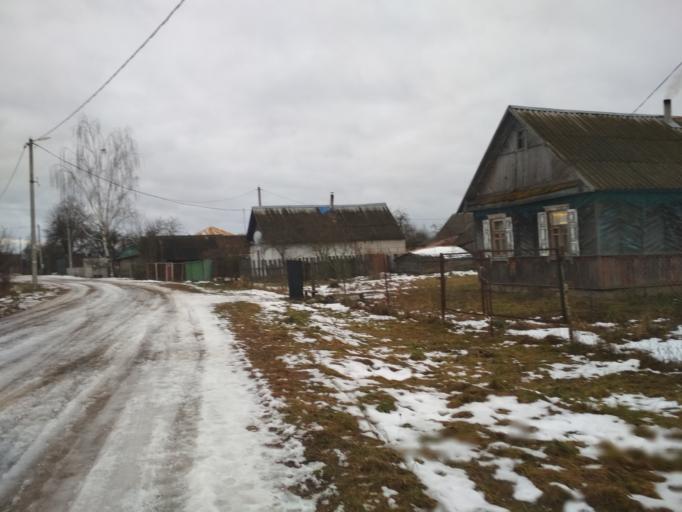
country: BY
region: Minsk
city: Mar''ina Horka
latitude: 53.5053
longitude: 28.0655
